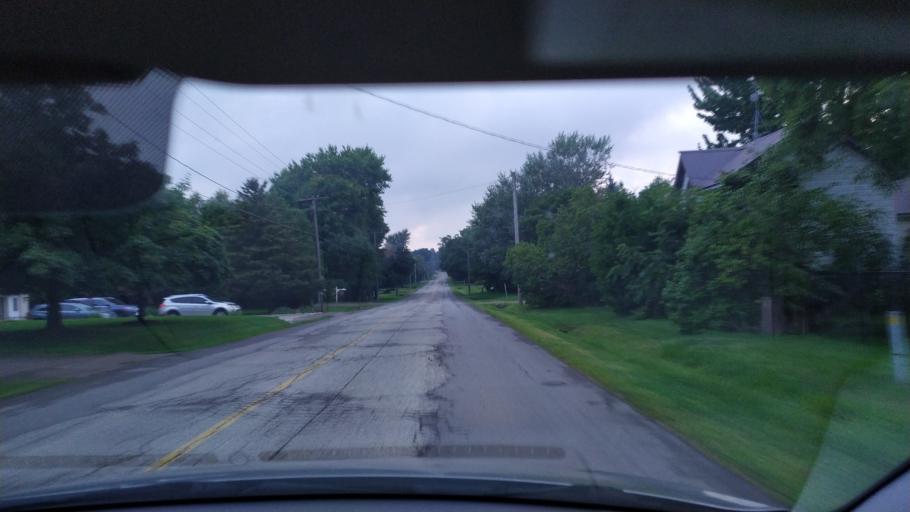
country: CA
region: Ontario
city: Kitchener
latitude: 43.3563
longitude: -80.6583
